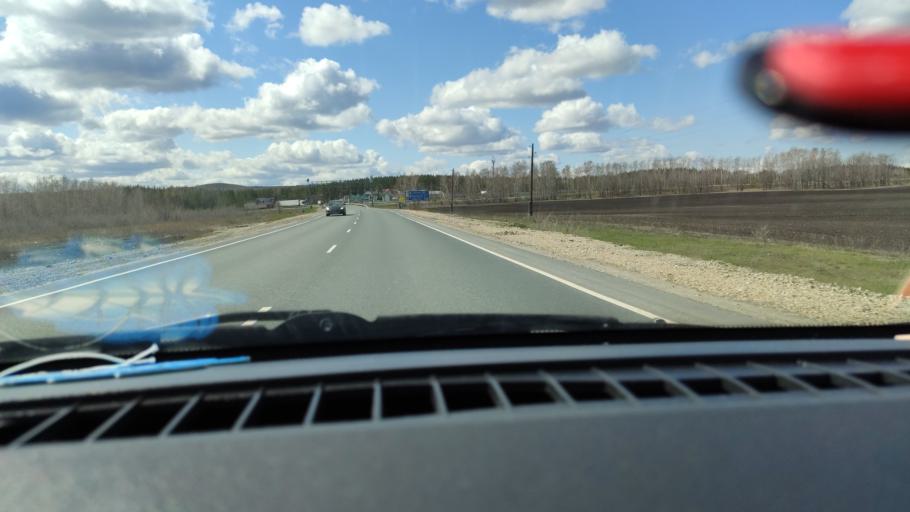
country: RU
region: Saratov
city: Khvalynsk
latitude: 52.5245
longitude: 48.0220
